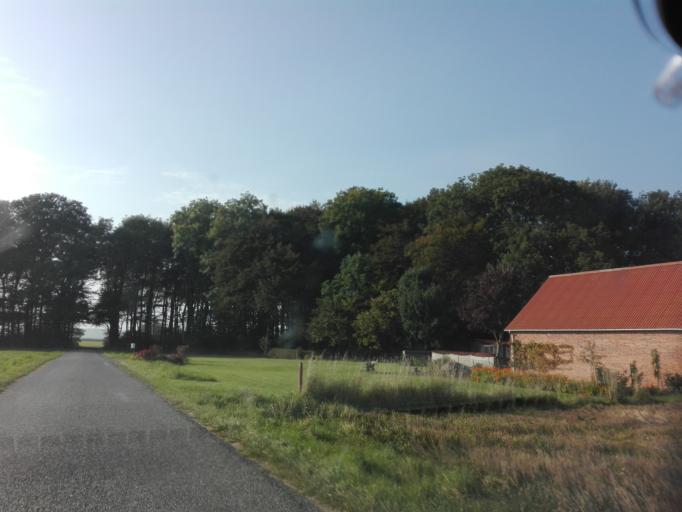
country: DK
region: Central Jutland
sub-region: Odder Kommune
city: Odder
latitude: 55.8724
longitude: 10.1540
